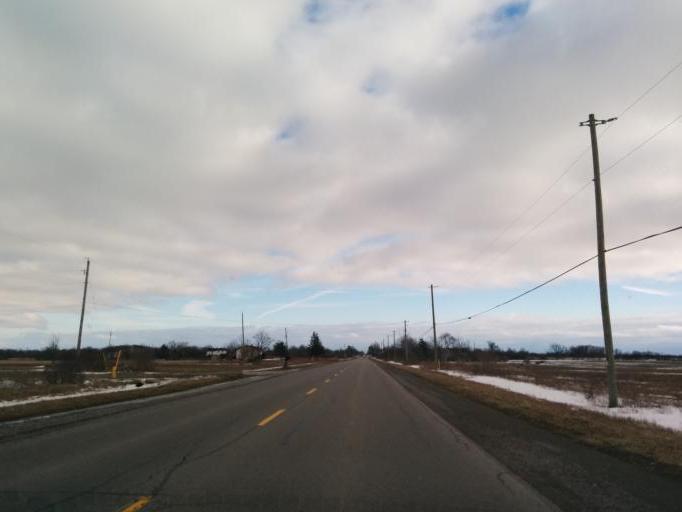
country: CA
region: Ontario
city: Brantford
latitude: 42.9705
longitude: -80.0749
